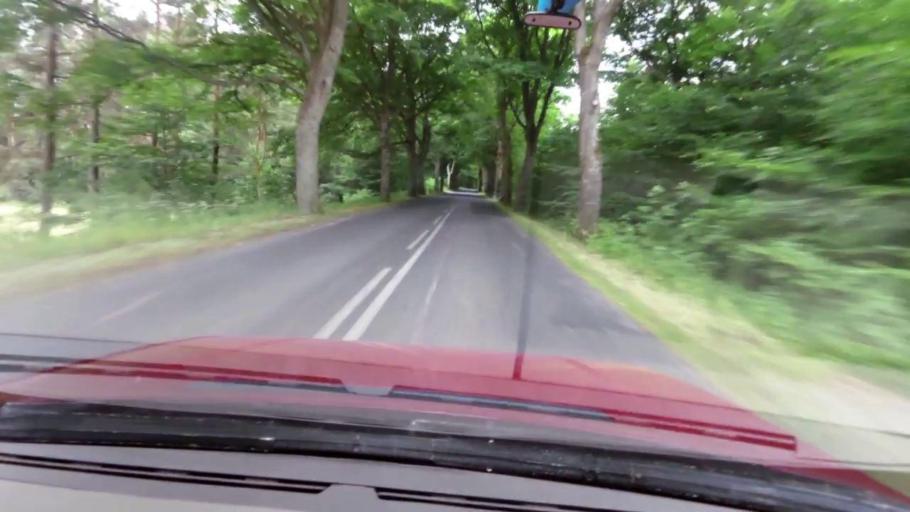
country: PL
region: West Pomeranian Voivodeship
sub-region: Powiat koszalinski
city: Polanow
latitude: 54.1269
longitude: 16.6380
